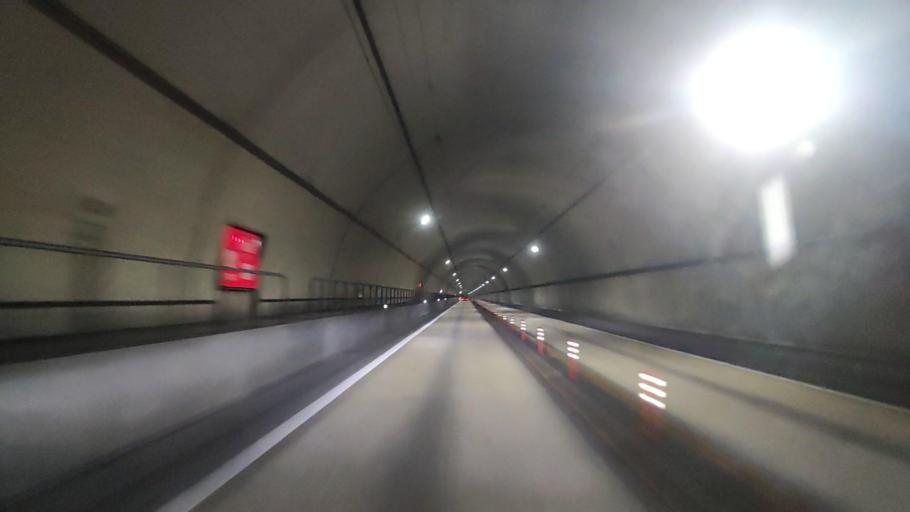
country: JP
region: Wakayama
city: Tanabe
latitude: 33.5701
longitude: 135.4844
